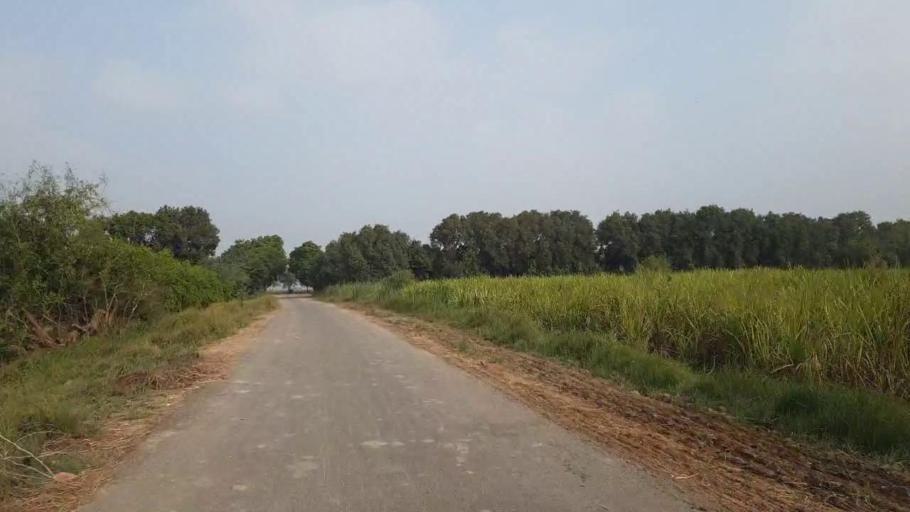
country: PK
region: Sindh
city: Tando Muhammad Khan
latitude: 25.1308
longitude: 68.5866
